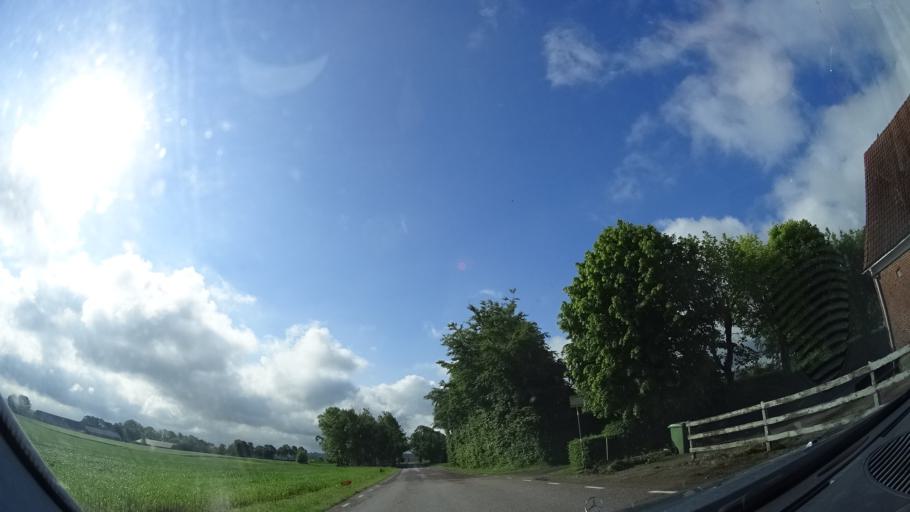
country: SE
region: Skane
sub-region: Eslovs Kommun
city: Stehag
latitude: 55.9162
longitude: 13.3854
